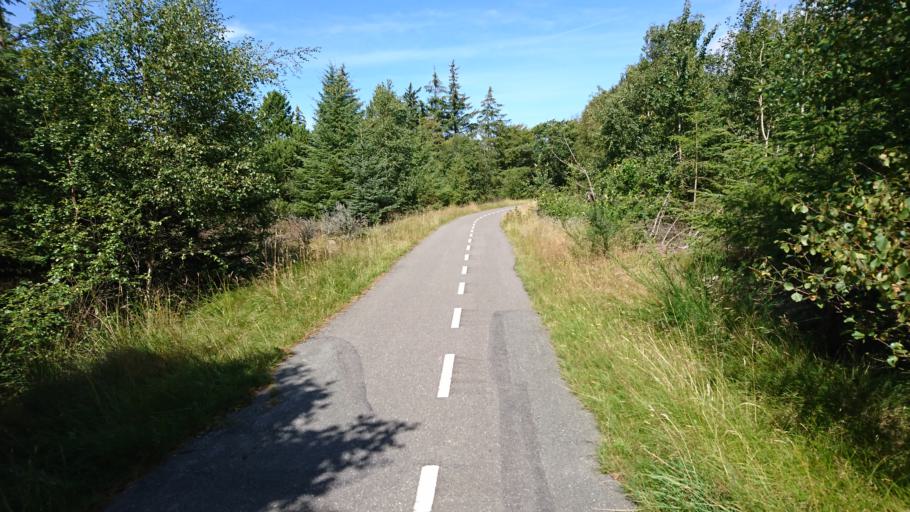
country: DK
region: South Denmark
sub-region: Fano Kommune
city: Nordby
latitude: 55.3969
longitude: 8.4221
